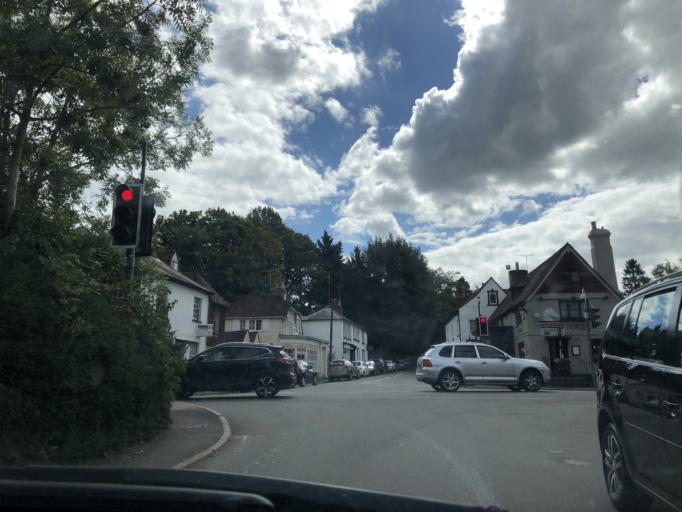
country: GB
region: England
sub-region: Kent
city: Halstead
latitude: 51.2784
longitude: 0.1274
